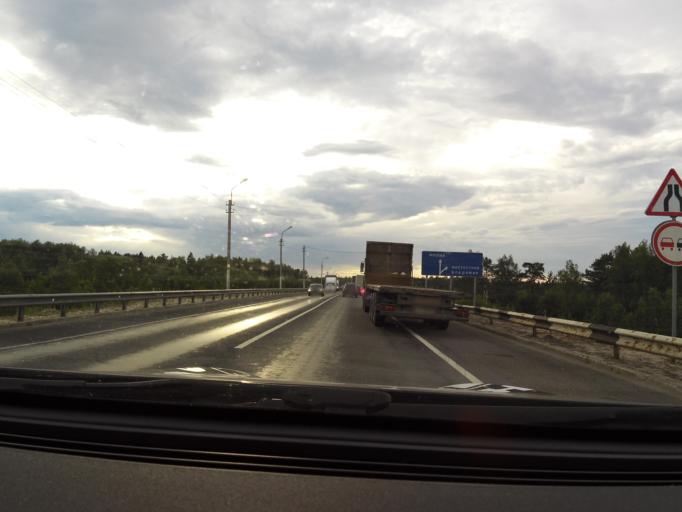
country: RU
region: Vladimir
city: Raduzhnyy
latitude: 56.0625
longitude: 40.3710
